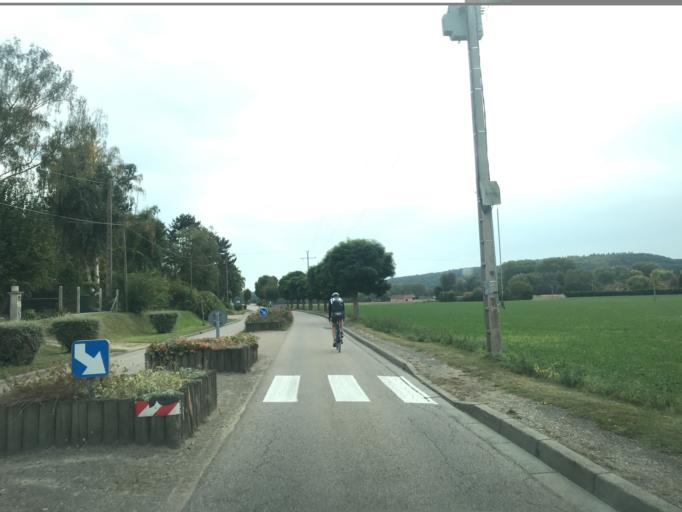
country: FR
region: Haute-Normandie
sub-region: Departement de l'Eure
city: Acquigny
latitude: 49.1923
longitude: 1.1833
